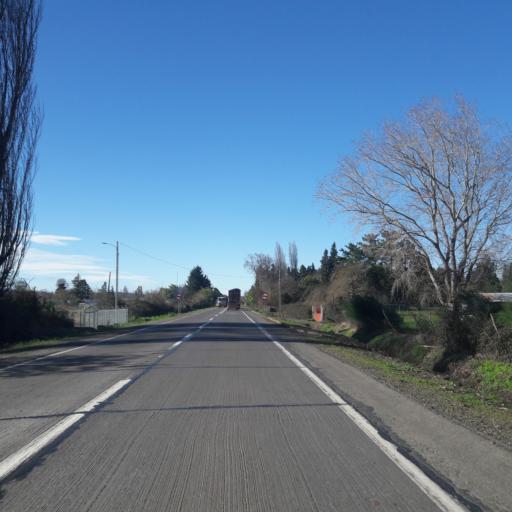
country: CL
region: Araucania
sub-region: Provincia de Malleco
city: Angol
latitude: -37.7723
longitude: -72.5492
